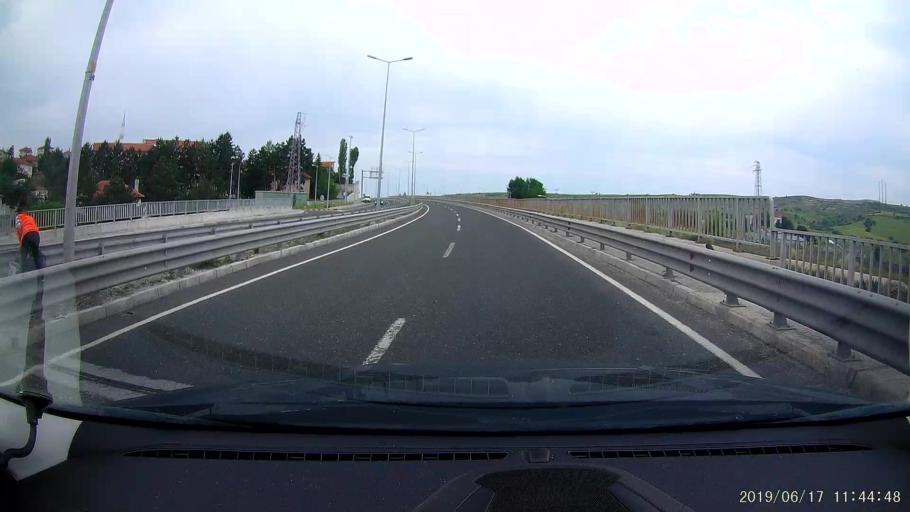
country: TR
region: Cankiri
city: Kursunlu
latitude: 40.8446
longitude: 33.2599
